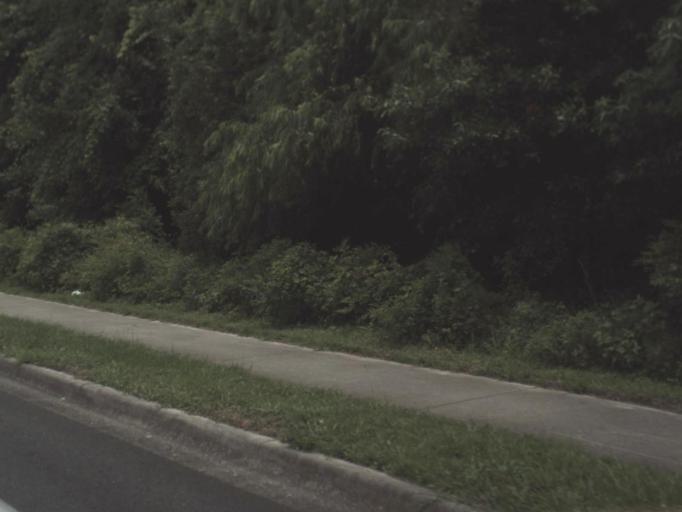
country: US
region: Florida
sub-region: Alachua County
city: Gainesville
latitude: 29.6442
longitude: -82.3726
